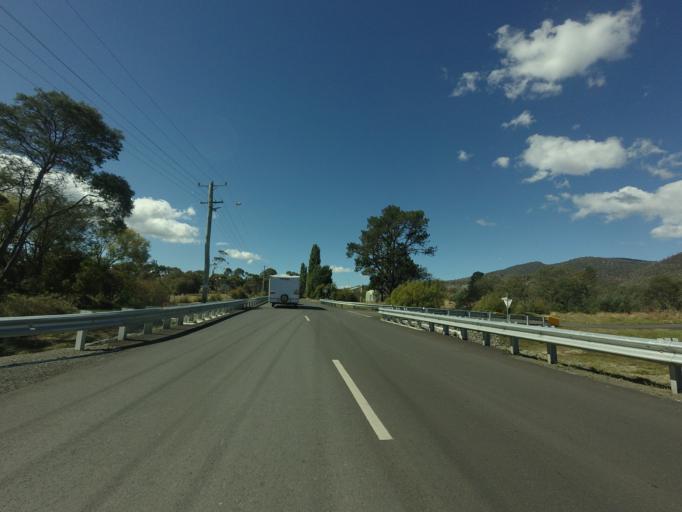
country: AU
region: Tasmania
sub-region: Break O'Day
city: St Helens
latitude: -41.6355
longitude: 147.9806
